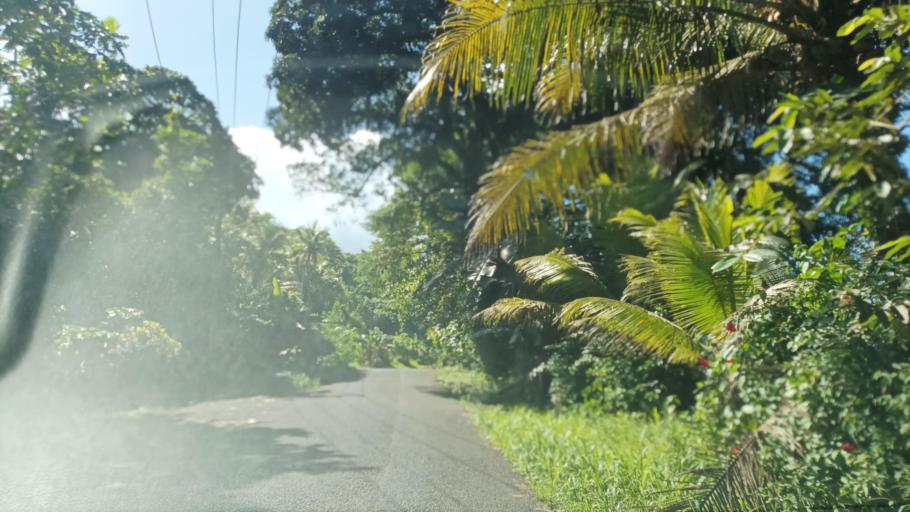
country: FM
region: Pohnpei
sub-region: Madolenihm Municipality
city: Madolenihm Municipality Government
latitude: 6.8516
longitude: 158.2978
